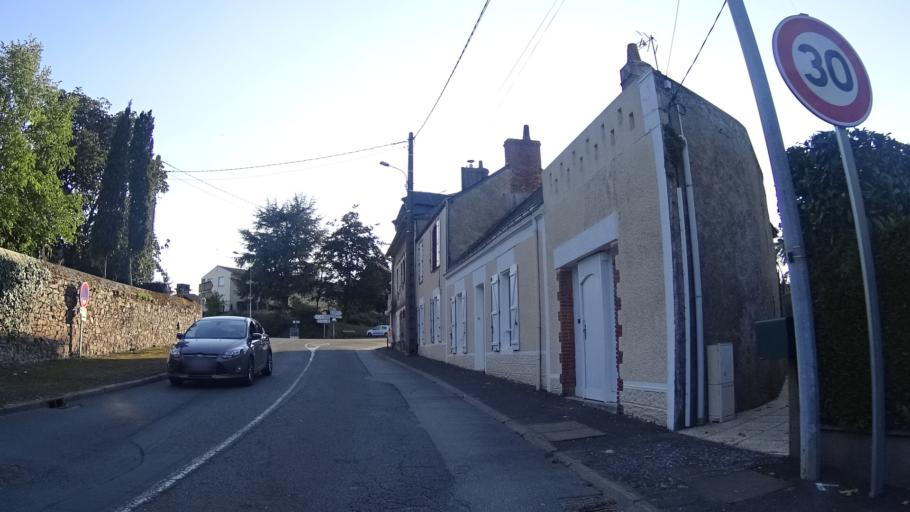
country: FR
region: Pays de la Loire
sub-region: Departement de Maine-et-Loire
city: Champtoceaux
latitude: 47.3377
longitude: -1.2618
